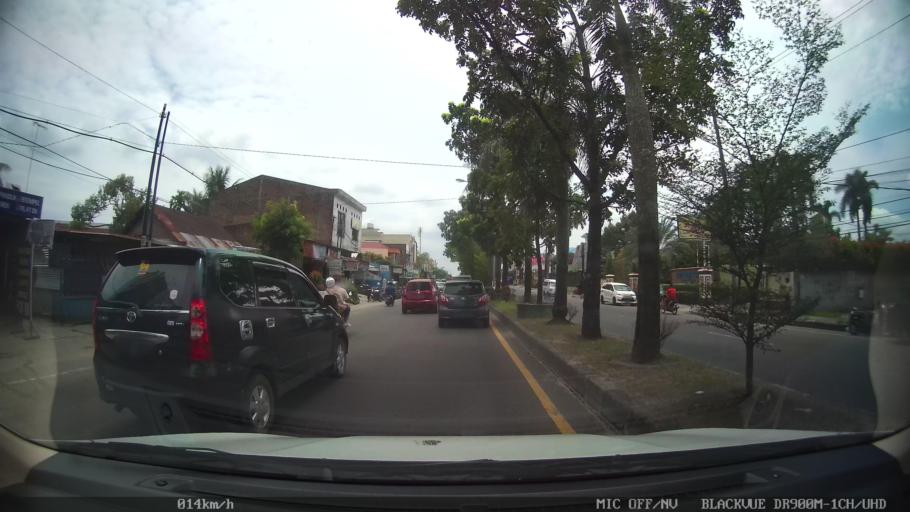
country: ID
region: North Sumatra
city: Deli Tua
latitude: 3.5287
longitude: 98.6367
